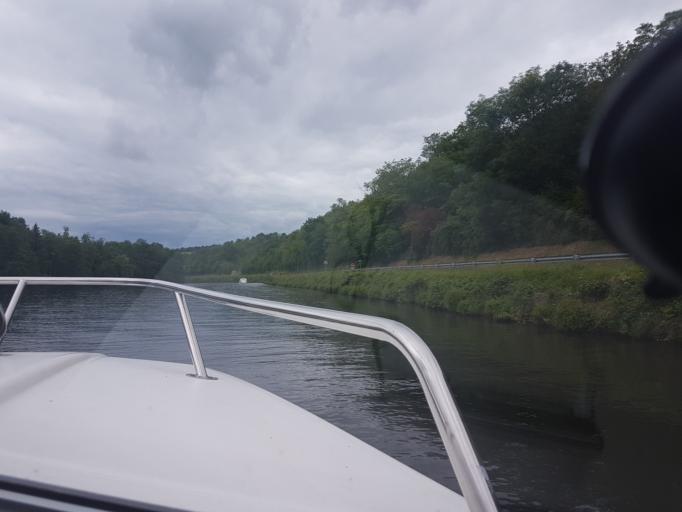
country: FR
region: Bourgogne
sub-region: Departement de l'Yonne
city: Champs-sur-Yonne
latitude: 47.7508
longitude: 3.5883
